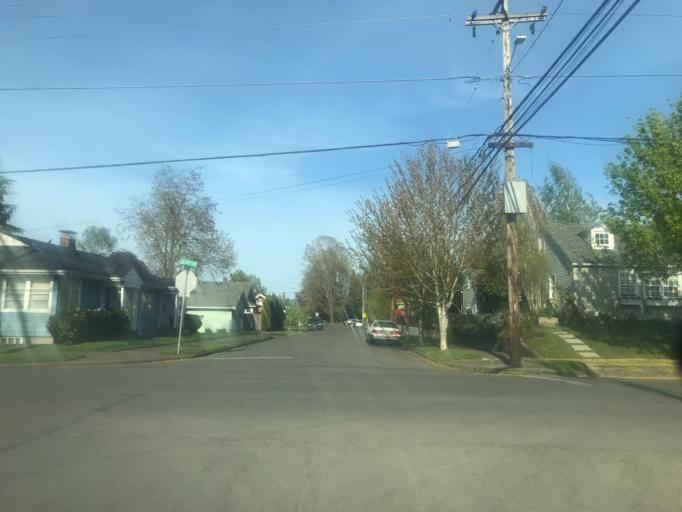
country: US
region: Oregon
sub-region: Multnomah County
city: Lents
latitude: 45.5035
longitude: -122.5854
